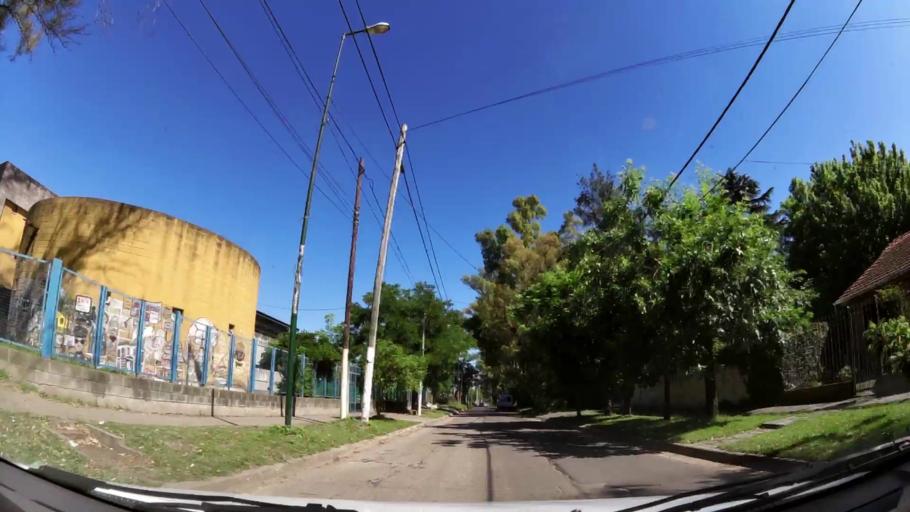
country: AR
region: Buenos Aires
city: Ituzaingo
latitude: -34.6245
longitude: -58.6608
